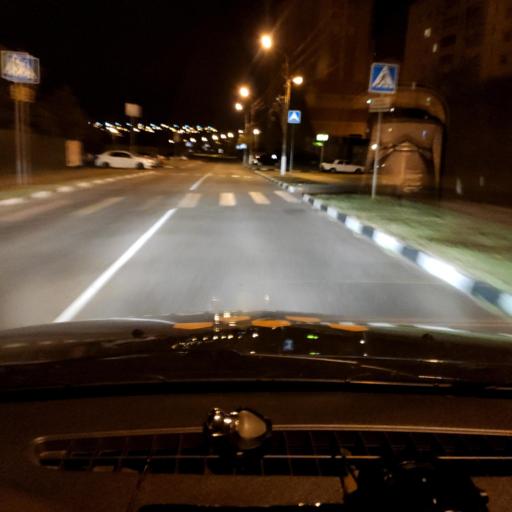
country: RU
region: Belgorod
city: Mayskiy
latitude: 50.5200
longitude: 36.4542
